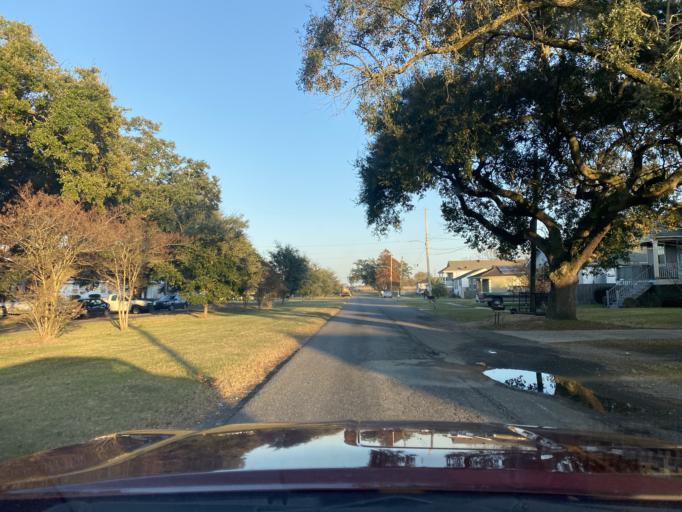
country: US
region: Louisiana
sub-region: Orleans Parish
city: New Orleans
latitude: 30.0226
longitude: -90.0503
